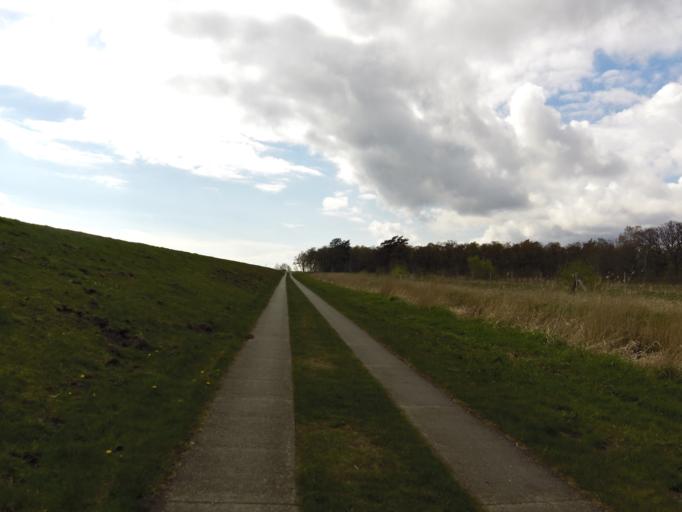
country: DE
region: Mecklenburg-Vorpommern
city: Barth
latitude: 54.4172
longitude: 12.7669
